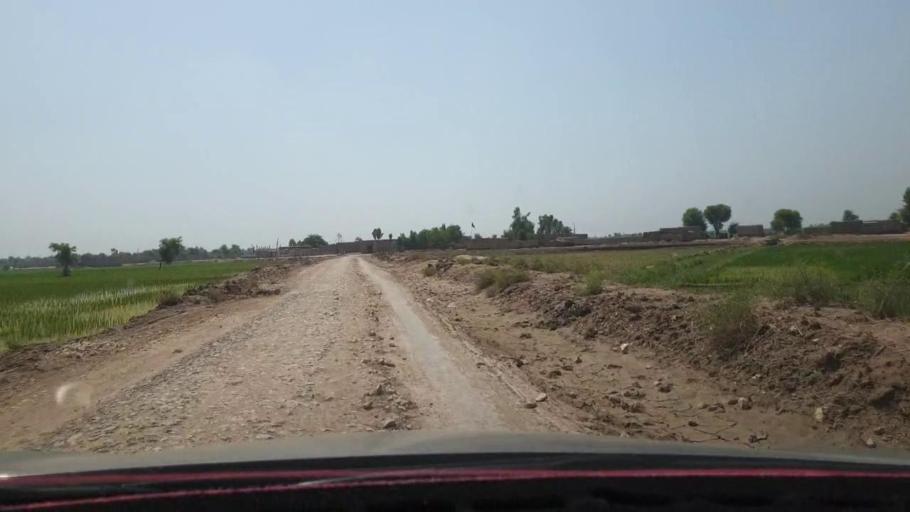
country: PK
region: Sindh
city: Warah
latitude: 27.4879
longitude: 67.8209
